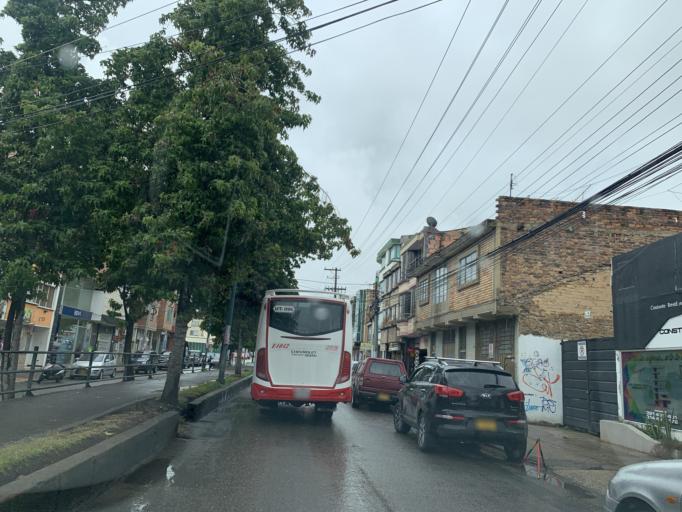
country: CO
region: Boyaca
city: Tunja
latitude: 5.5257
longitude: -73.3655
